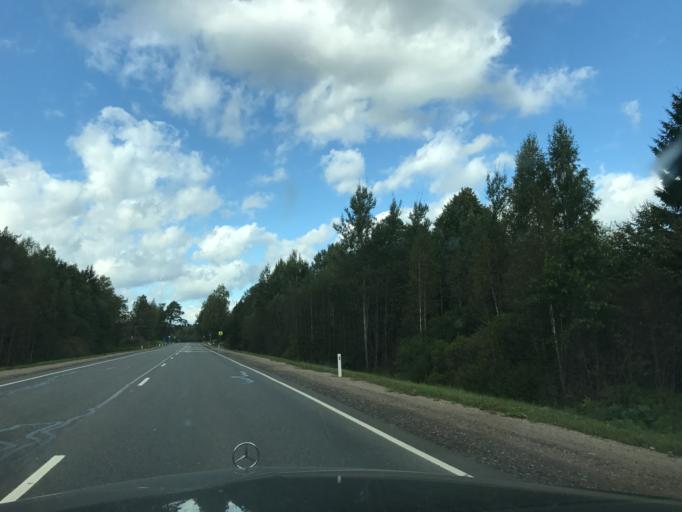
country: RU
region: Pskov
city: Opochka
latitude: 56.5986
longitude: 28.8614
